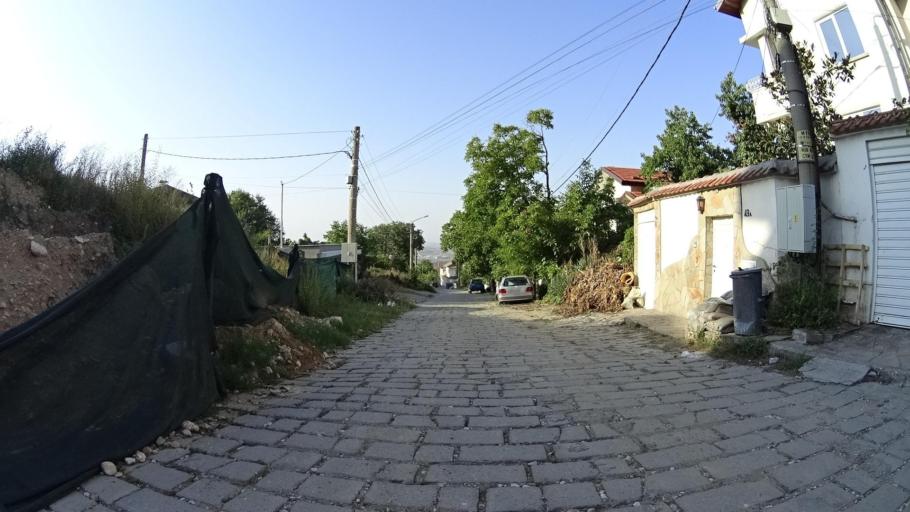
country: BG
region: Plovdiv
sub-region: Obshtina Plovdiv
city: Plovdiv
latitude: 42.0618
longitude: 24.6996
